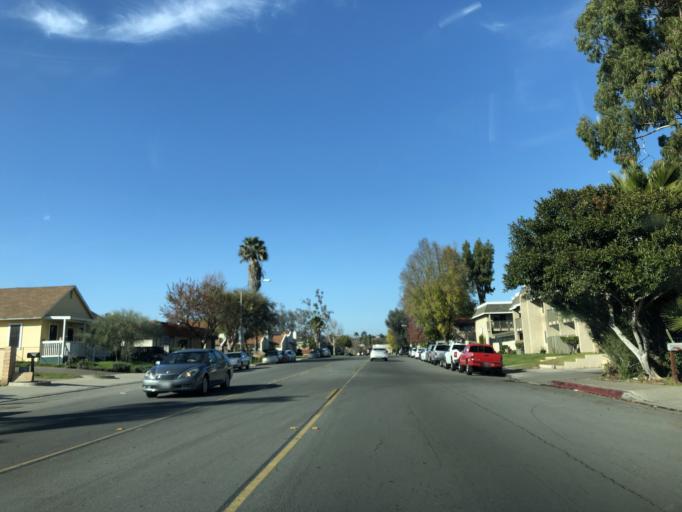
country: US
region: California
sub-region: San Diego County
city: Escondido
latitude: 33.1339
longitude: -117.0915
